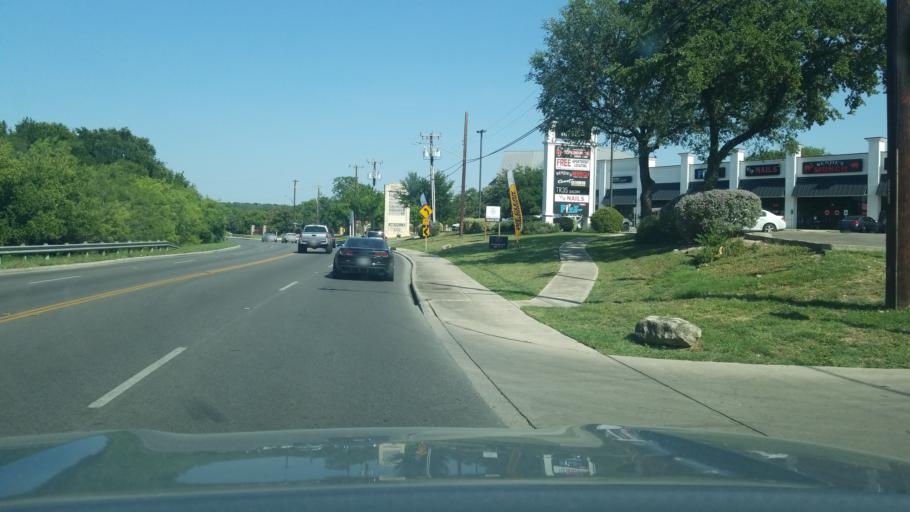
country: US
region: Texas
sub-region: Bexar County
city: Hollywood Park
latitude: 29.5789
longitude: -98.5126
